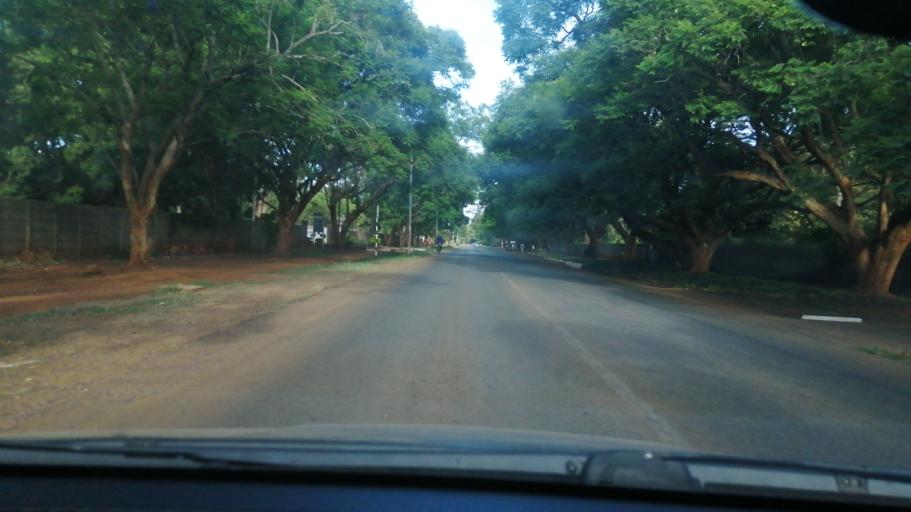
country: ZW
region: Harare
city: Harare
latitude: -17.7622
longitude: 31.0776
